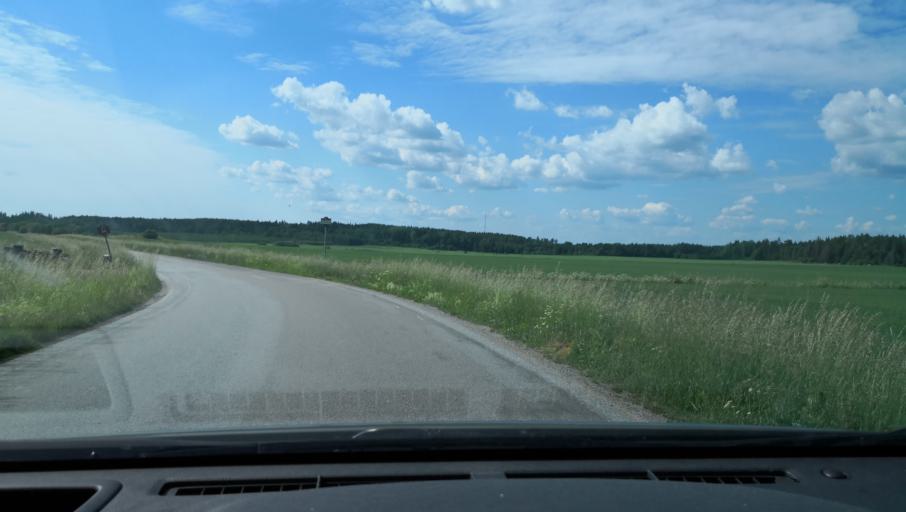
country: SE
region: Uppsala
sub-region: Enkopings Kommun
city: Orsundsbro
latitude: 59.8128
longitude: 17.3824
